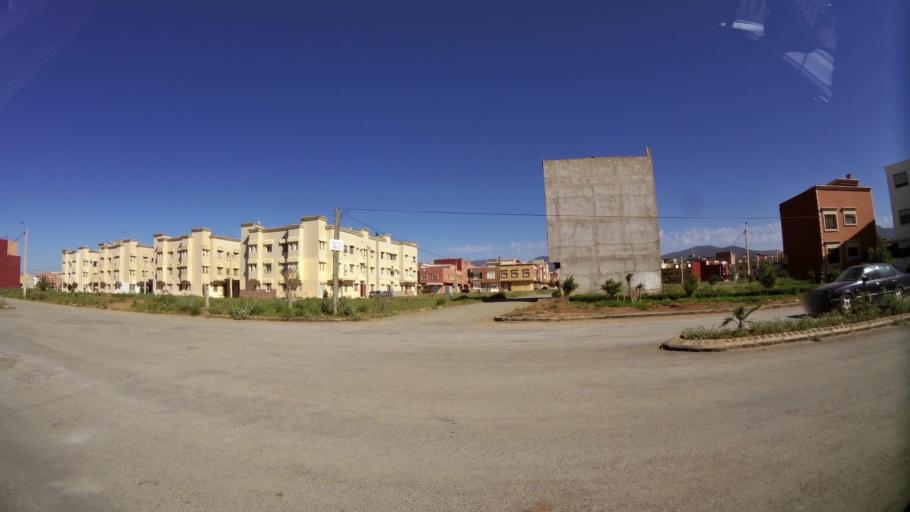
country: MA
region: Oriental
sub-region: Berkane-Taourirt
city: Berkane
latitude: 34.9414
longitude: -2.3381
